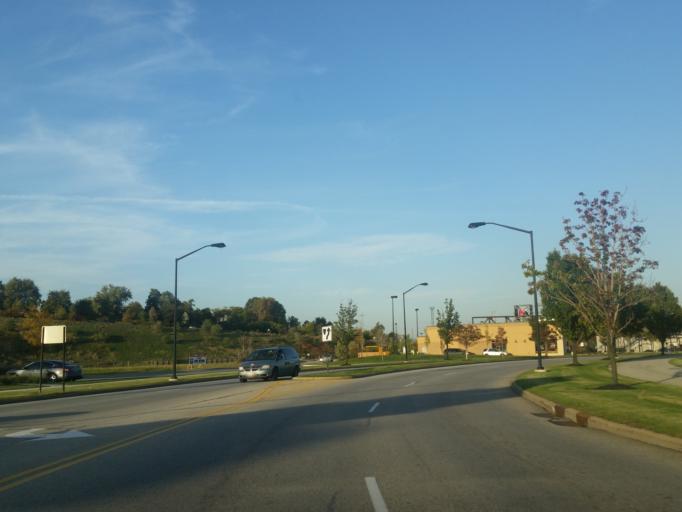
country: US
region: Ohio
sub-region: Cuyahoga County
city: Newburgh Heights
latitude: 41.4630
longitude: -81.6900
